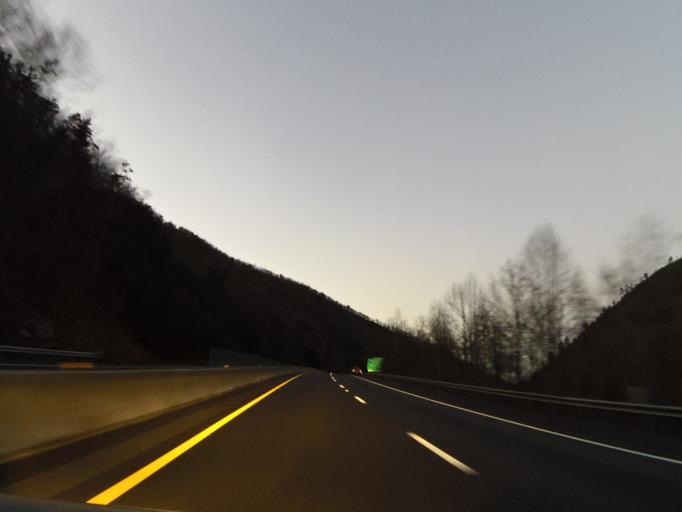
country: US
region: Tennessee
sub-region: Cocke County
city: Newport
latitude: 35.8221
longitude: -83.1824
